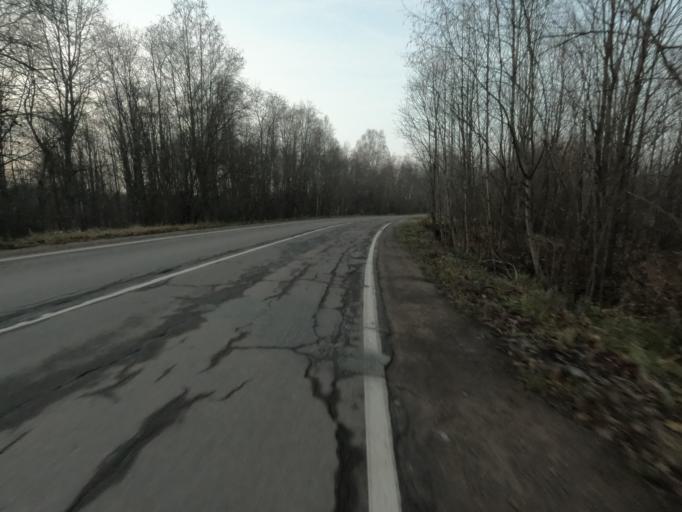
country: RU
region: Leningrad
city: Kirovsk
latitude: 59.8578
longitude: 30.9860
